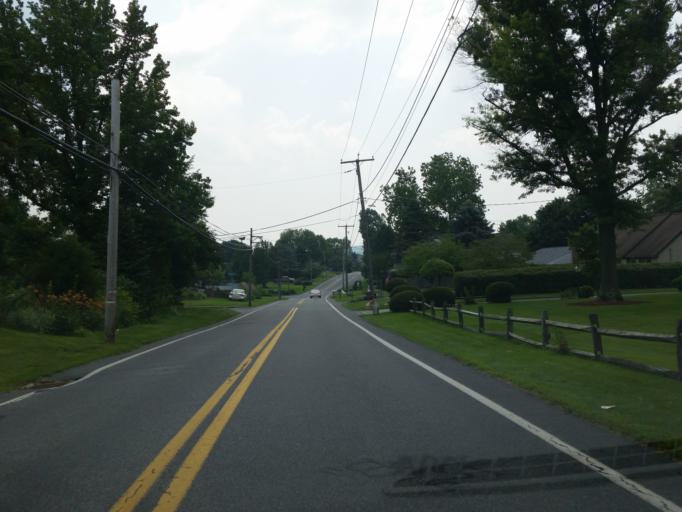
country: US
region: Pennsylvania
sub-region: Dauphin County
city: Palmdale
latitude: 40.2959
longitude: -76.6047
